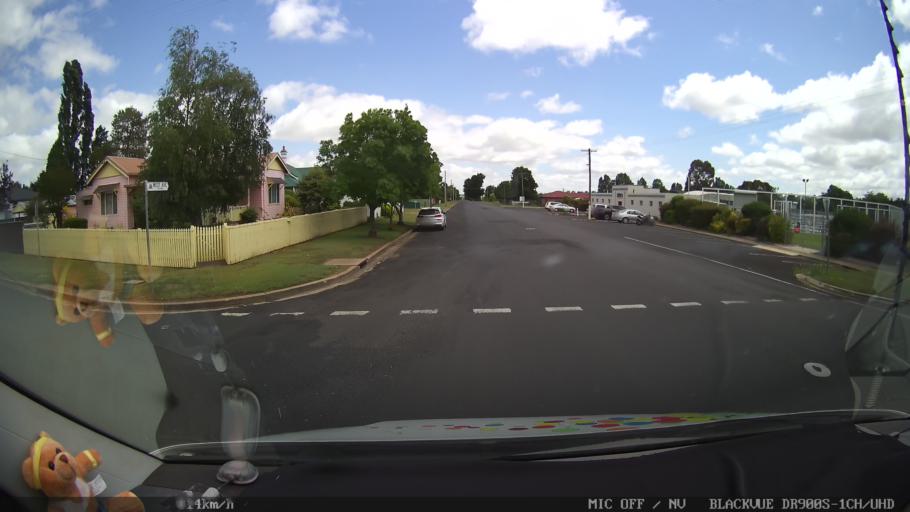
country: AU
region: New South Wales
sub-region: Glen Innes Severn
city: Glen Innes
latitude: -29.7329
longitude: 151.7332
